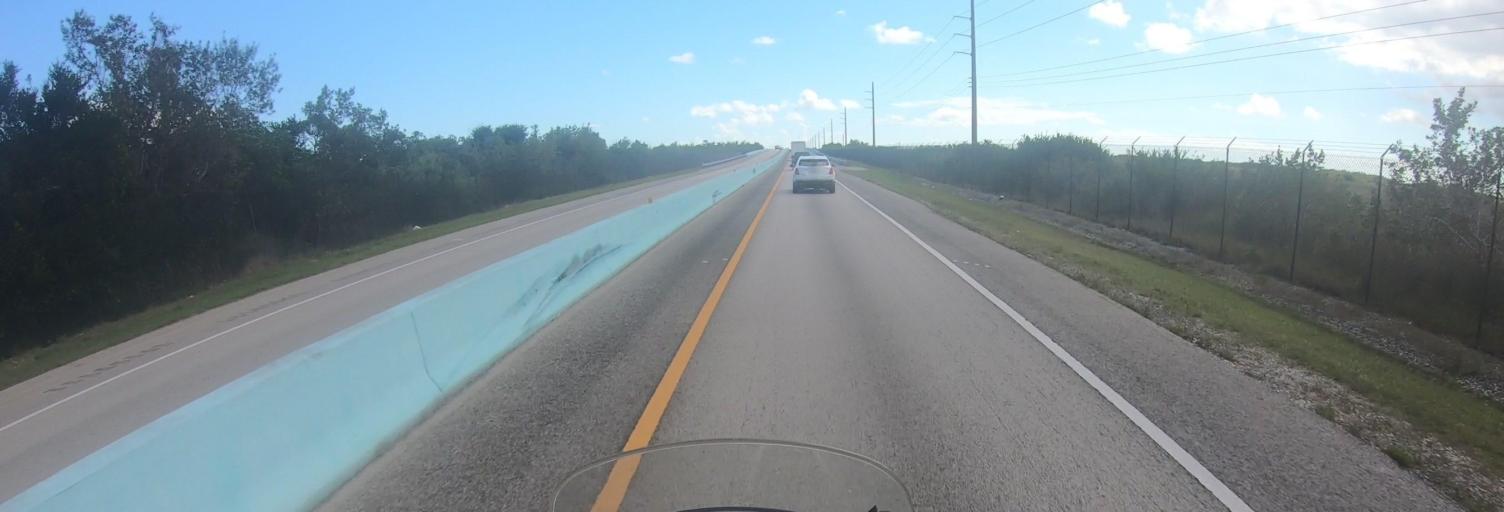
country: US
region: Florida
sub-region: Miami-Dade County
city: Florida City
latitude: 25.3350
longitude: -80.4547
